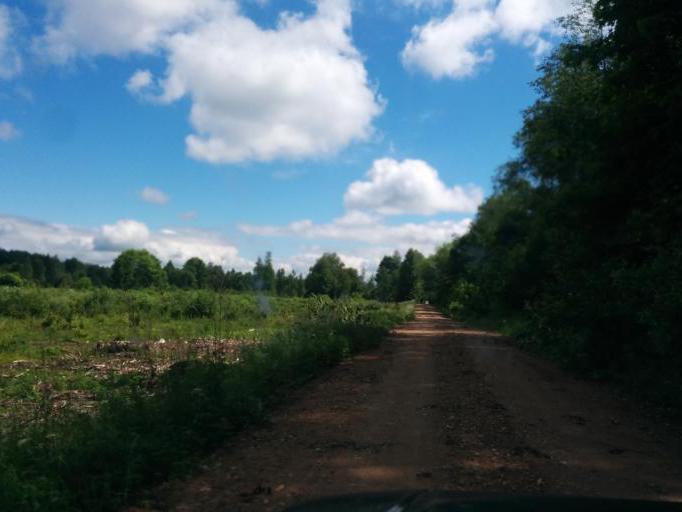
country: LV
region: Vilaka
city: Vilaka
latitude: 57.3362
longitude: 27.7196
